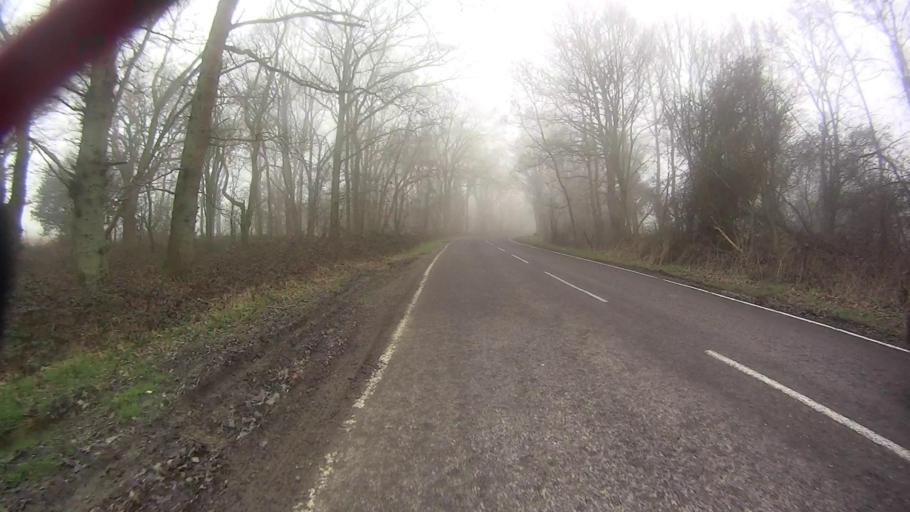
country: GB
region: England
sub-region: Surrey
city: Newdigate
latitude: 51.1426
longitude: -0.3213
